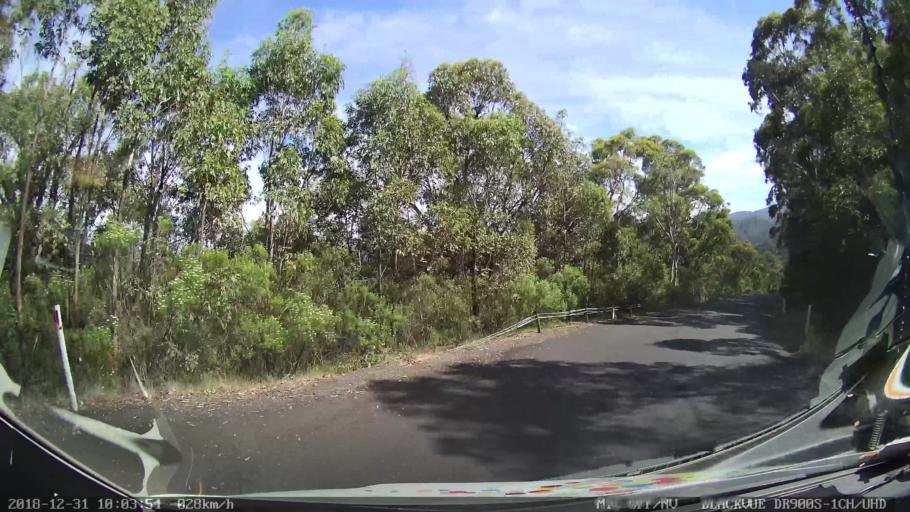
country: AU
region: New South Wales
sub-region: Snowy River
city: Jindabyne
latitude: -36.5339
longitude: 148.1894
